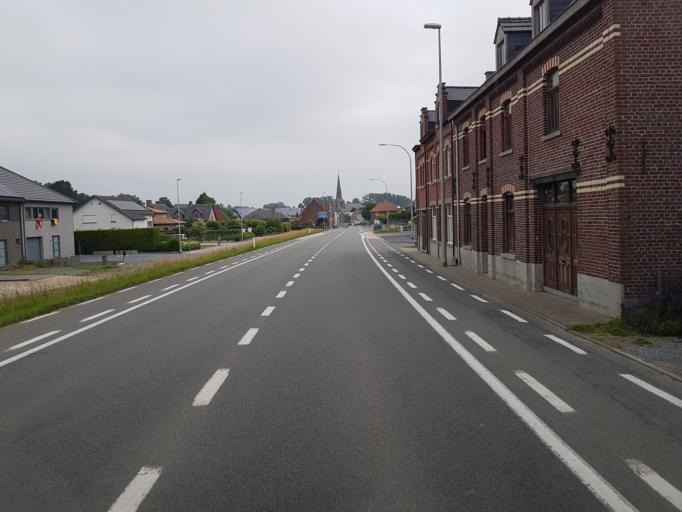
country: BE
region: Flanders
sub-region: Provincie Oost-Vlaanderen
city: Ninove
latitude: 50.8393
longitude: 3.9532
